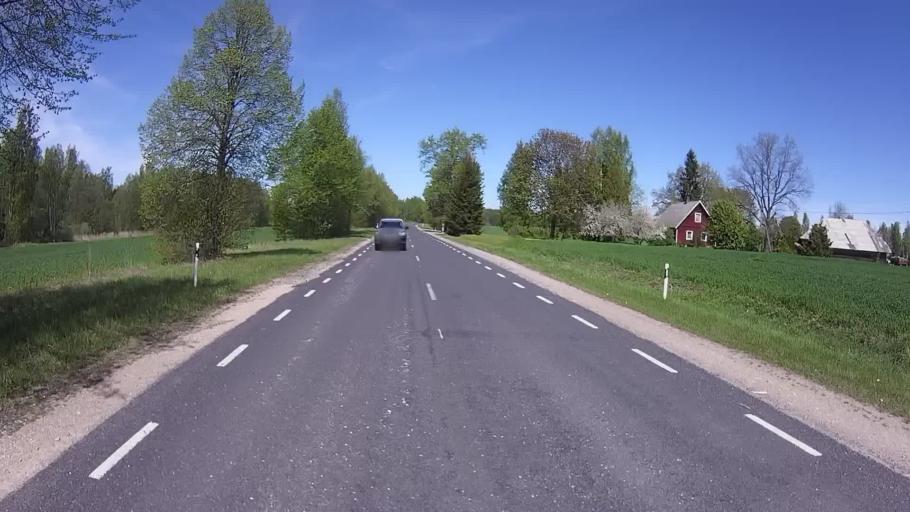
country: EE
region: Polvamaa
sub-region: Raepina vald
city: Rapina
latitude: 58.0445
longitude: 27.3896
